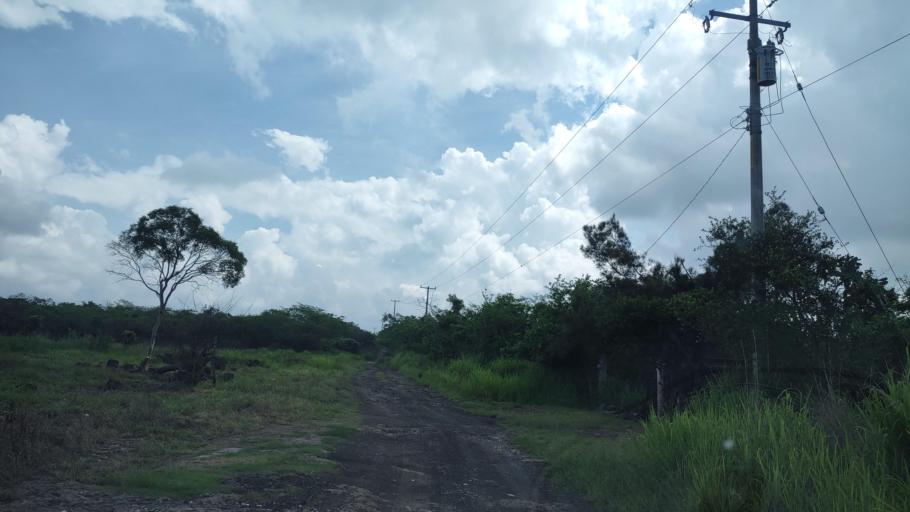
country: MX
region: Veracruz
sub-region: Emiliano Zapata
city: Dos Rios
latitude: 19.4545
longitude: -96.8086
